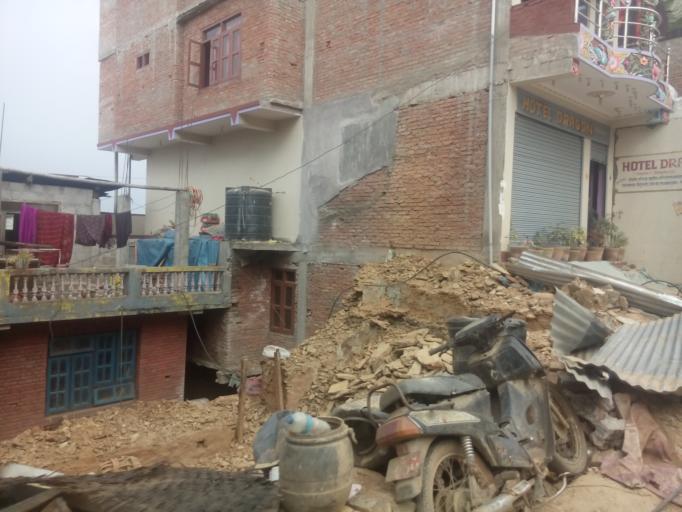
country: NP
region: Central Region
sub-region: Bagmati Zone
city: Nagarkot
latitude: 27.7727
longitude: 85.7188
